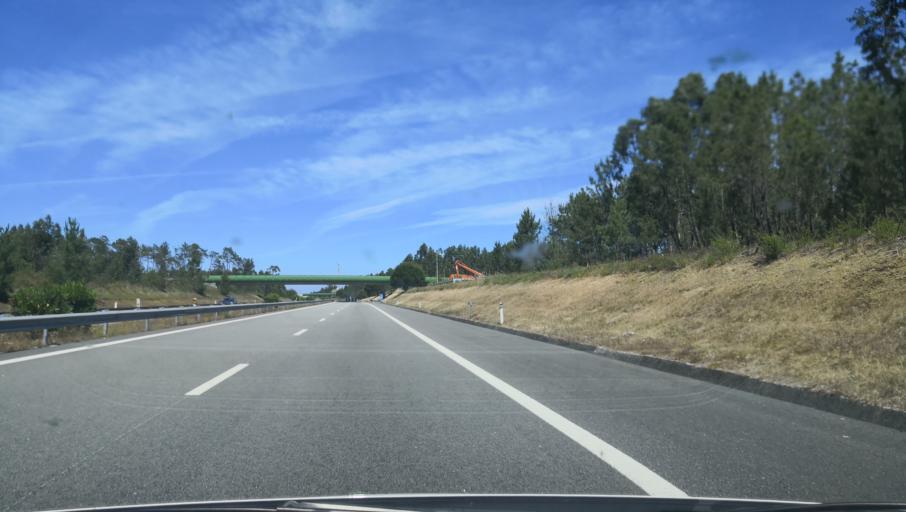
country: PT
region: Coimbra
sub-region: Montemor-O-Velho
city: Arazede
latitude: 40.2532
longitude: -8.6424
